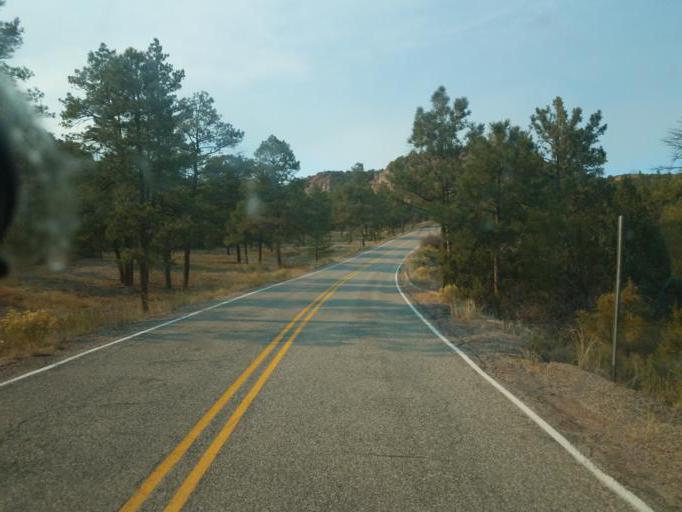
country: US
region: New Mexico
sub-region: Los Alamos County
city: White Rock
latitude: 35.8045
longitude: -106.2471
